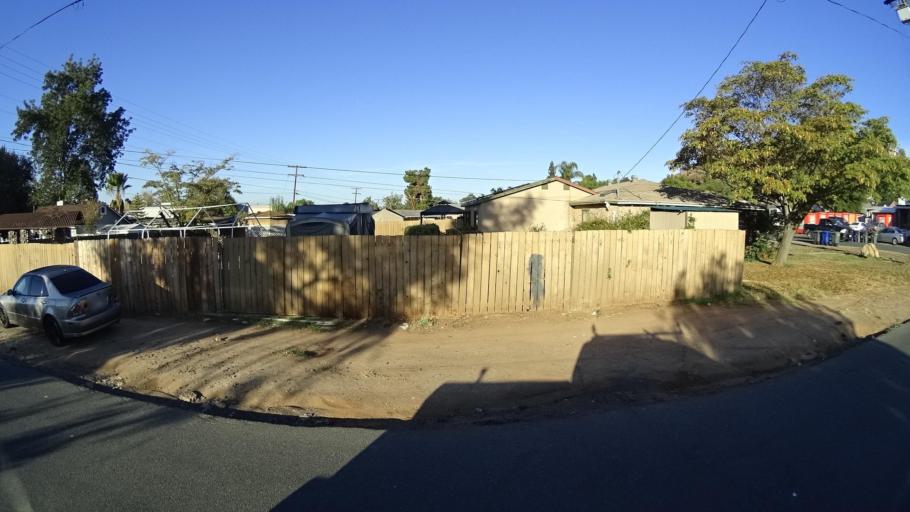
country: US
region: California
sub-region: San Diego County
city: Bostonia
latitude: 32.8140
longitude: -116.9402
